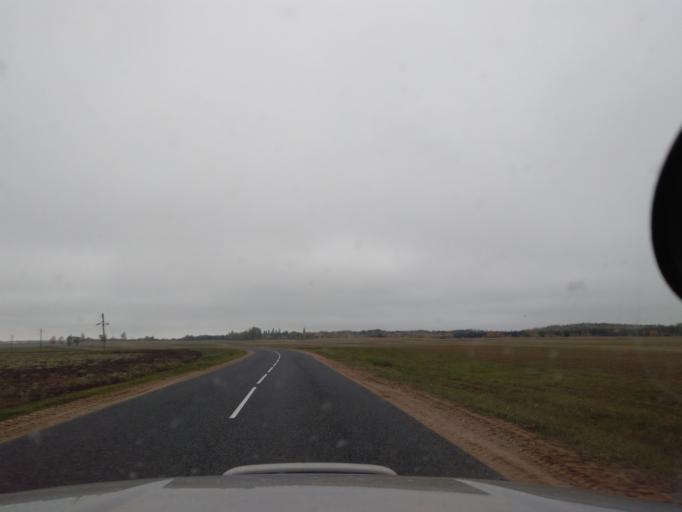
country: BY
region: Minsk
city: Kapyl'
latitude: 53.1537
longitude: 27.1827
